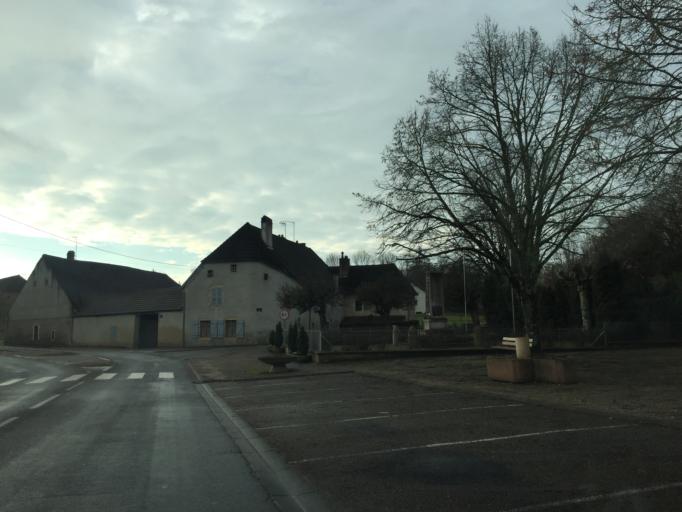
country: FR
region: Franche-Comte
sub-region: Departement du Jura
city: Mont-sous-Vaudrey
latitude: 46.9790
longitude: 5.6024
